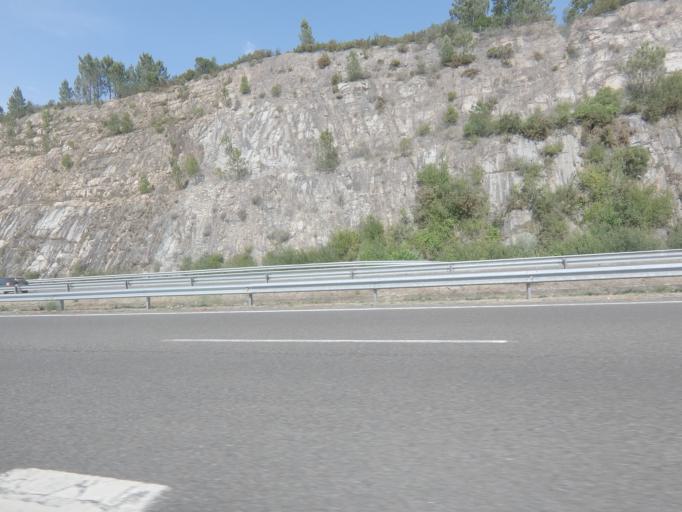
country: ES
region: Galicia
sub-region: Provincia de Ourense
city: Ourense
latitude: 42.2919
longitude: -7.8774
